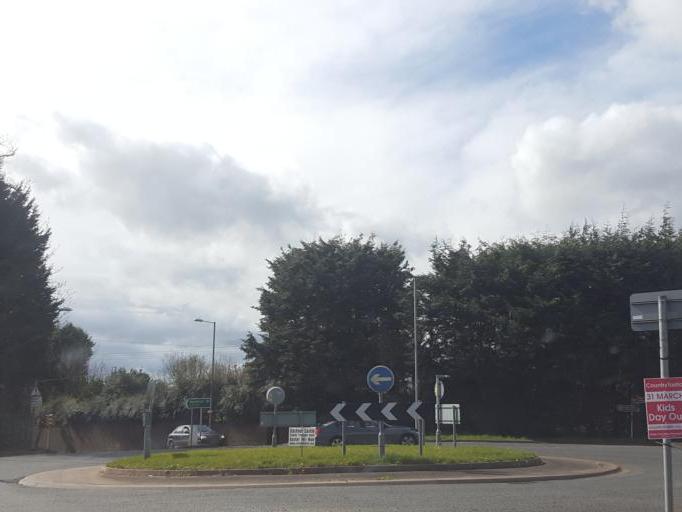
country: GB
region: England
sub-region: Worcestershire
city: Bransford
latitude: 52.1719
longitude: -2.2991
